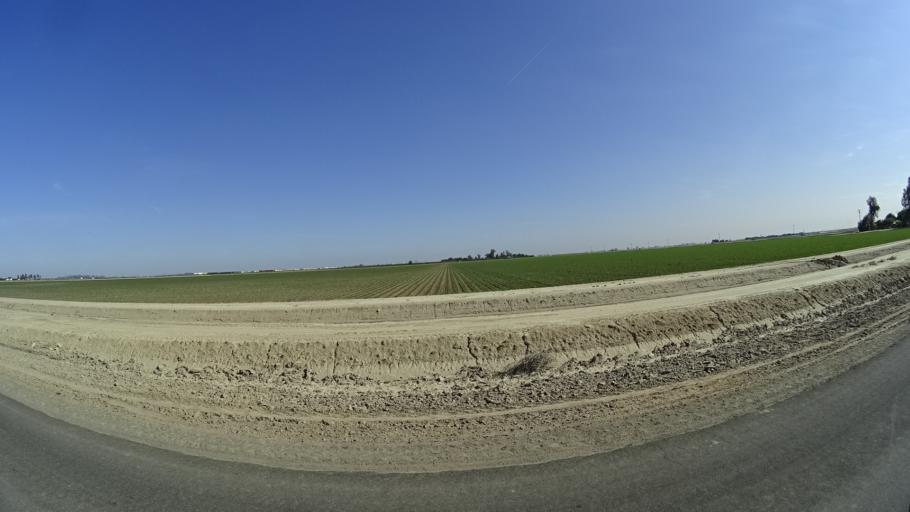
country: US
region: California
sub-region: Kings County
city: Home Garden
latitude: 36.2258
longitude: -119.6403
